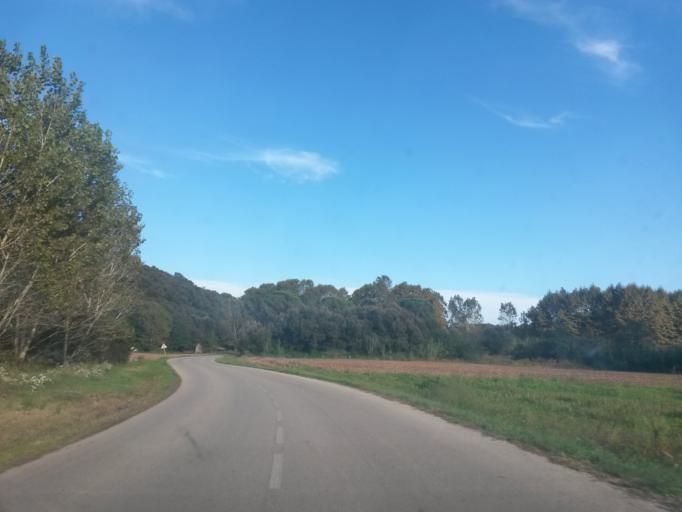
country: ES
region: Catalonia
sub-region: Provincia de Girona
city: Angles
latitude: 41.9638
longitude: 2.6486
